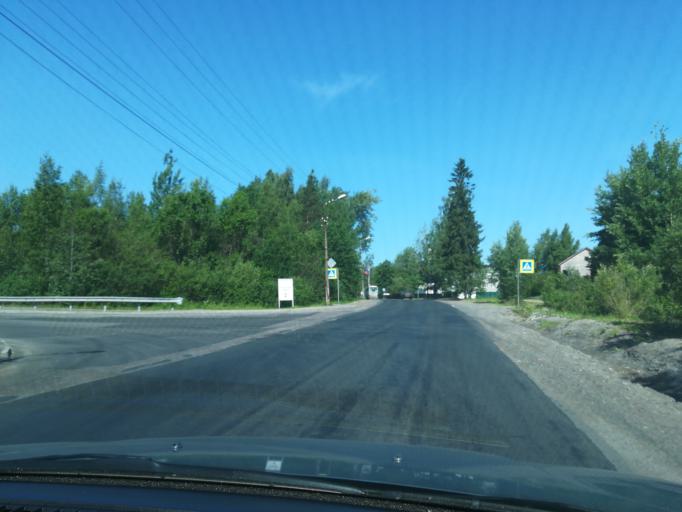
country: RU
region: Leningrad
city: Svetogorsk
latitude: 61.1059
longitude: 28.8659
